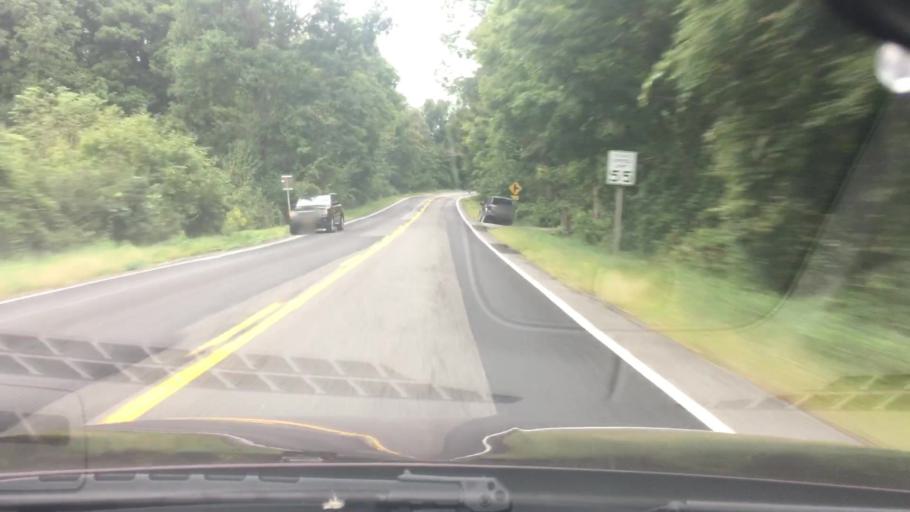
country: US
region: New York
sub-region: Dutchess County
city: Millbrook
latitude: 41.7939
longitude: -73.7074
